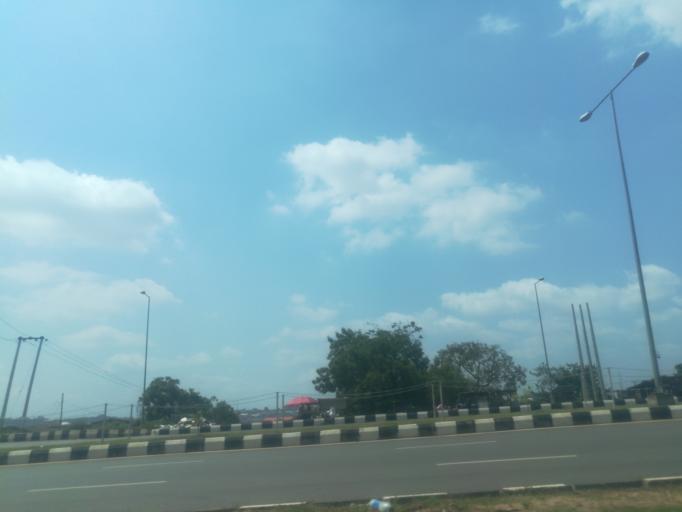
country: NG
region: Ogun
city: Abeokuta
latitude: 7.1453
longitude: 3.3623
